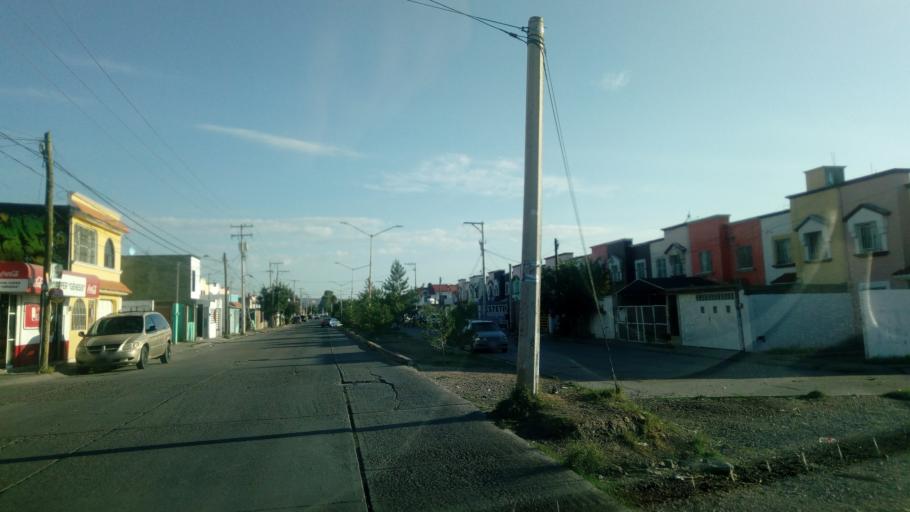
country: MX
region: Durango
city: Victoria de Durango
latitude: 24.0680
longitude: -104.5865
